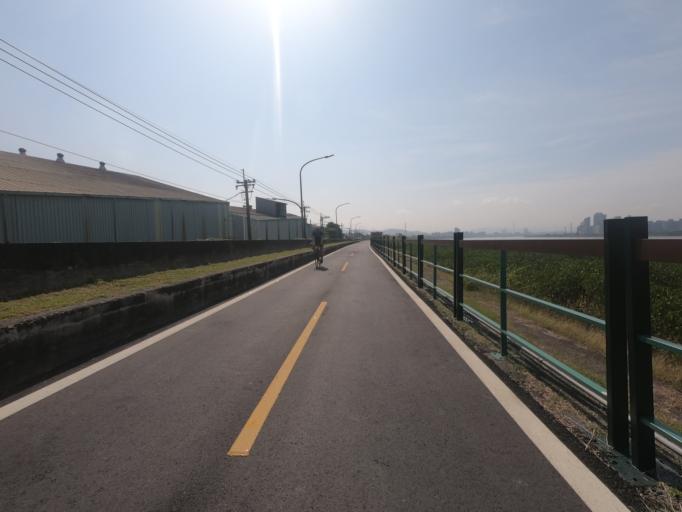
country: TW
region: Taipei
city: Taipei
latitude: 25.1043
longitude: 121.4794
